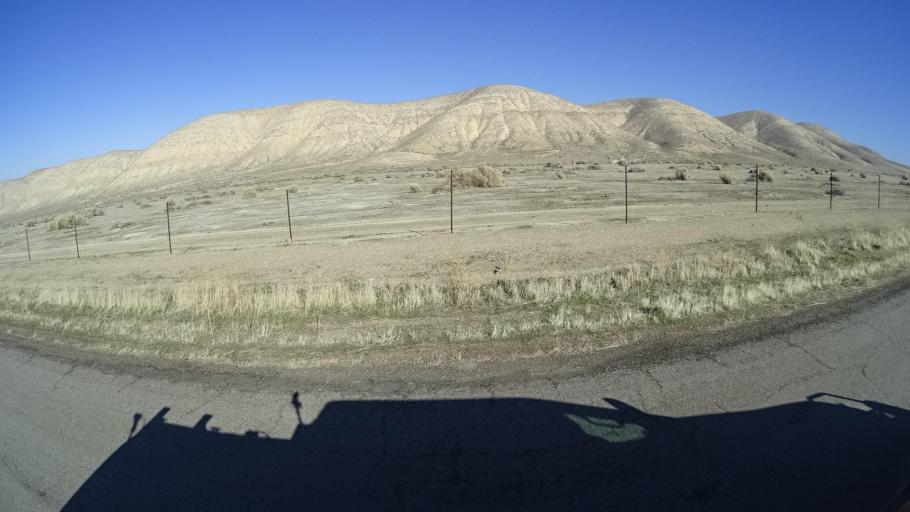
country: US
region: California
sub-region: Kern County
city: Maricopa
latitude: 35.0007
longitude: -119.4027
